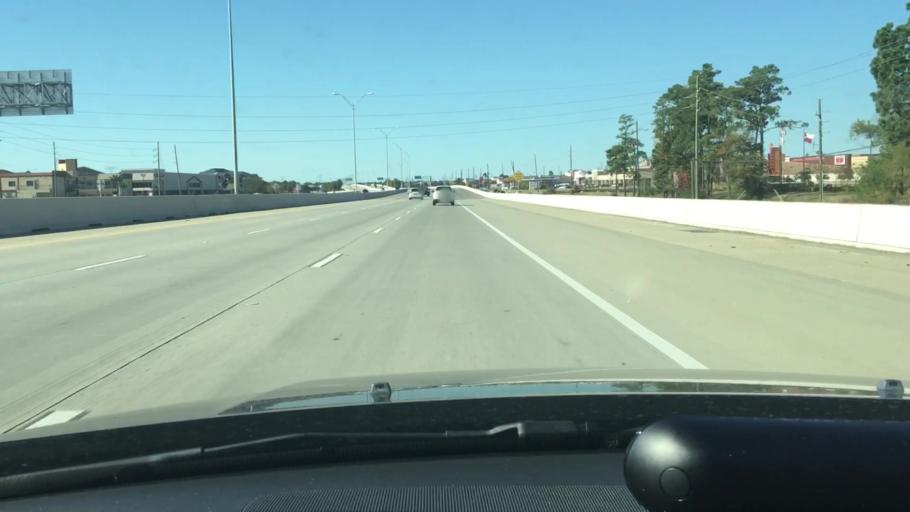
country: US
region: Texas
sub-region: Harris County
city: Humble
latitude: 29.9343
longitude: -95.2380
